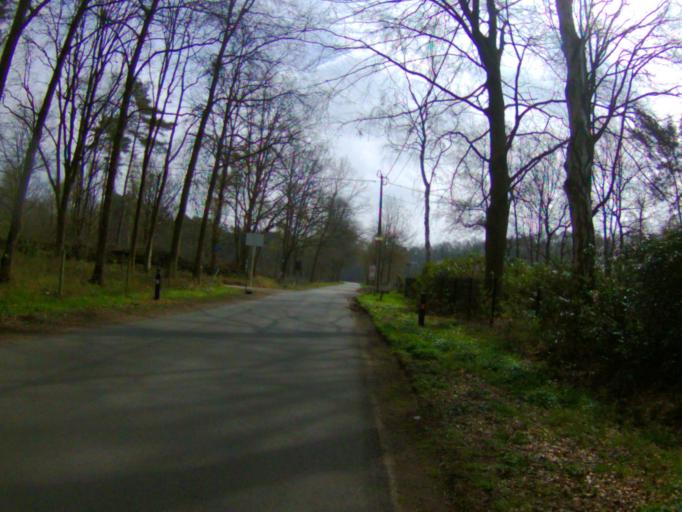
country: BE
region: Flanders
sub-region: Provincie Antwerpen
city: Nijlen
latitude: 51.1880
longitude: 4.6921
